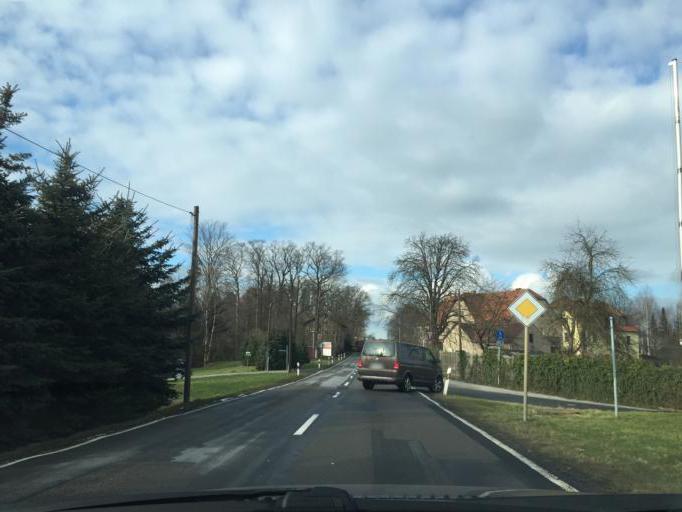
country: DE
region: Saxony
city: Wachau
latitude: 51.1411
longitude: 13.9137
